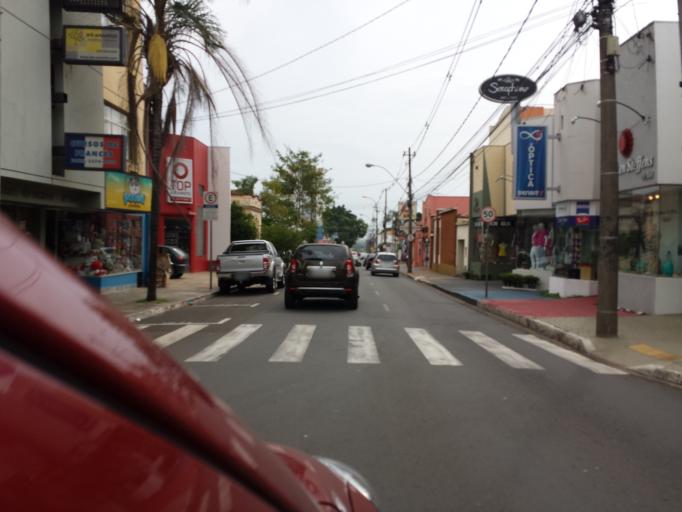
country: BR
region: Sao Paulo
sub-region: Sao Carlos
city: Sao Carlos
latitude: -22.0115
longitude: -47.8928
